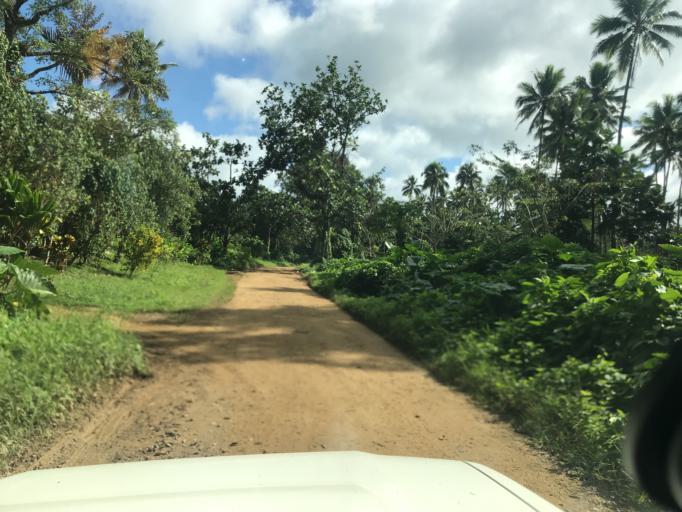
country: VU
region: Sanma
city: Luganville
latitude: -15.4767
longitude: 167.0862
